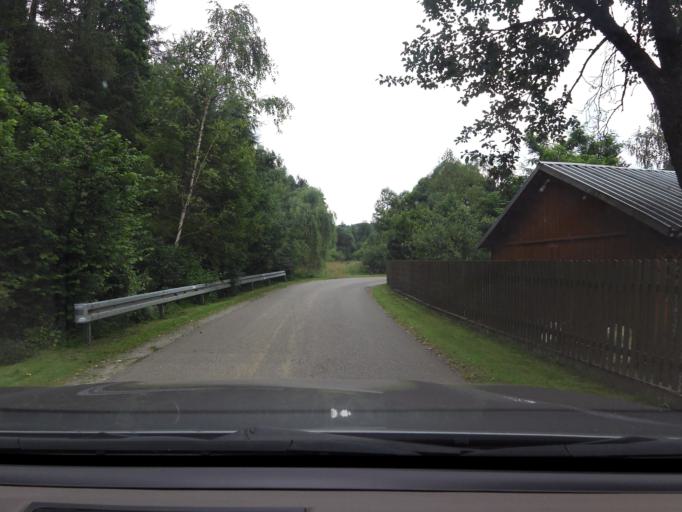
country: PL
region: Silesian Voivodeship
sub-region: Powiat zywiecki
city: Rajcza
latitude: 49.5048
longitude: 19.1156
